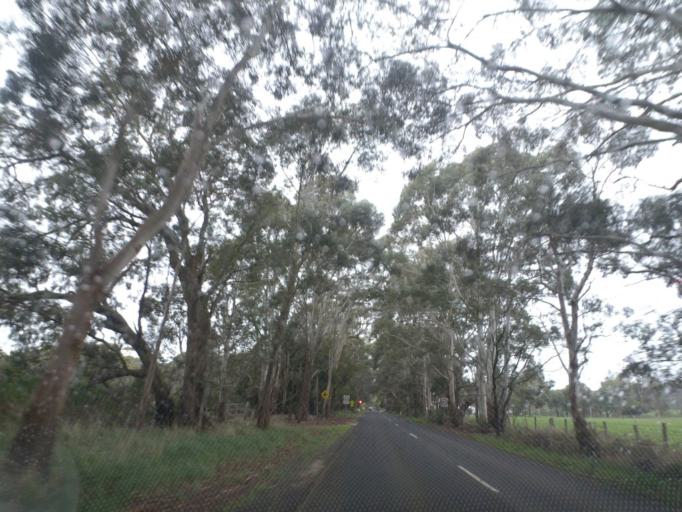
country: AU
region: Victoria
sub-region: Hume
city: Sunbury
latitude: -37.3472
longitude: 144.6172
